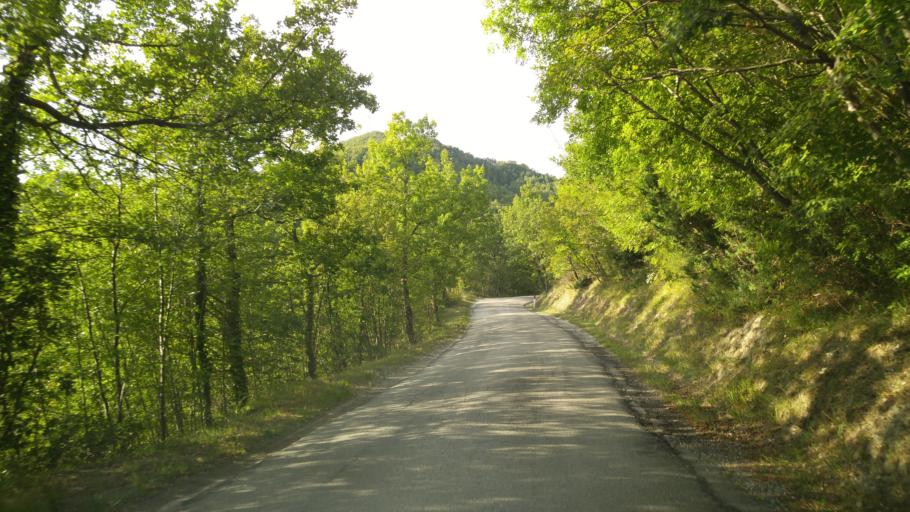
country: IT
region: The Marches
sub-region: Provincia di Pesaro e Urbino
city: Cagli
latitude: 43.5550
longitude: 12.6298
